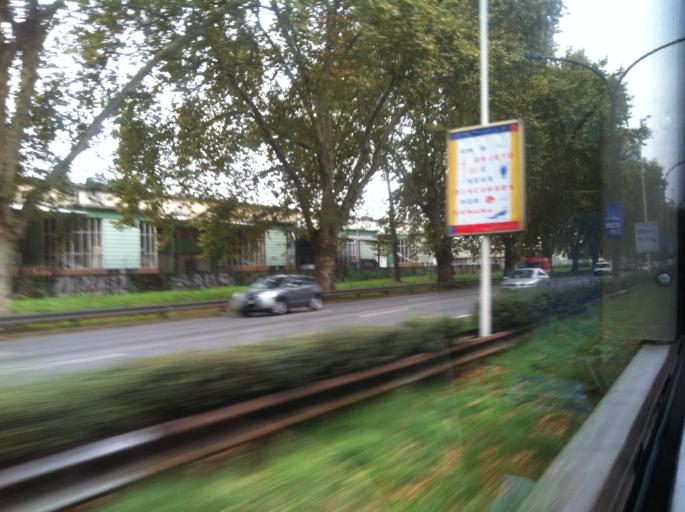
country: PT
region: Porto
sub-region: Matosinhos
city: Senhora da Hora
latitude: 41.1741
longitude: -8.6507
